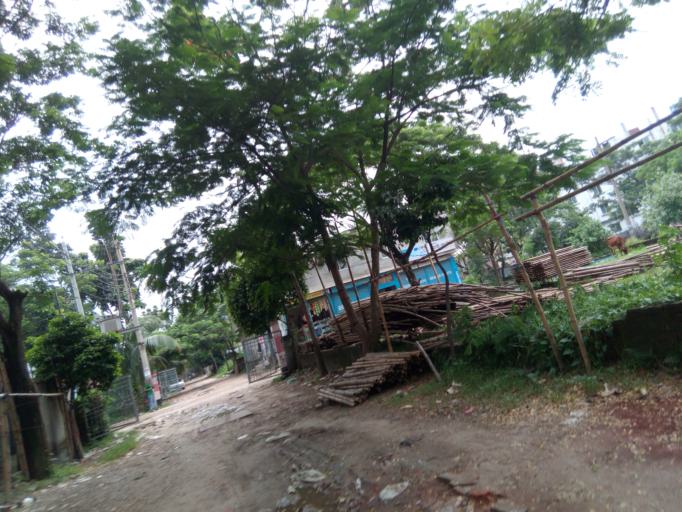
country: BD
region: Dhaka
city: Azimpur
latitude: 23.7467
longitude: 90.3493
